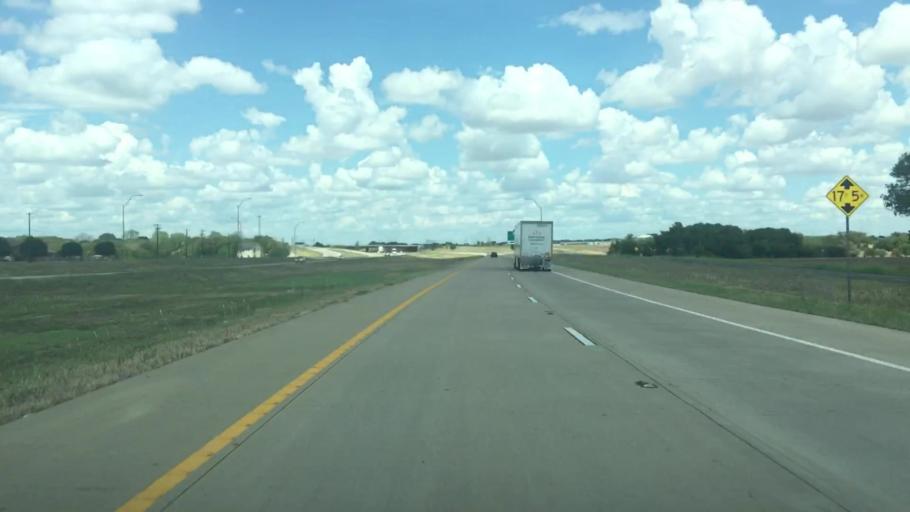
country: US
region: Texas
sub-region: Williamson County
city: Georgetown
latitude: 30.6331
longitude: -97.6279
